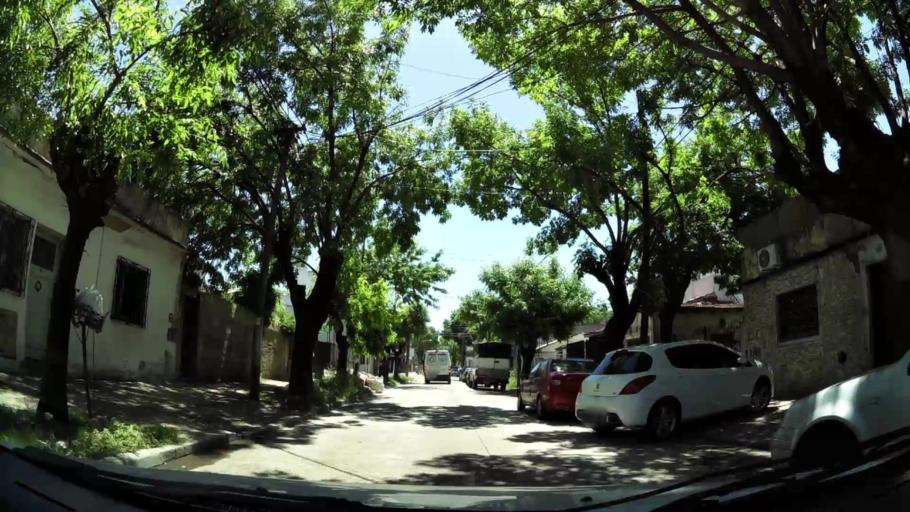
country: AR
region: Buenos Aires
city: Caseros
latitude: -34.5884
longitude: -58.5616
